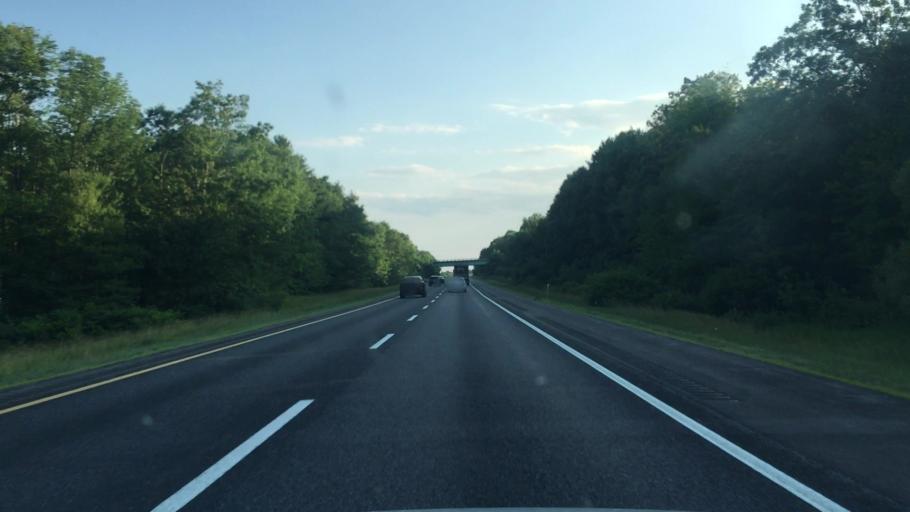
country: US
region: Maine
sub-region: Sagadahoc County
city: Richmond
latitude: 44.0339
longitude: -69.9078
